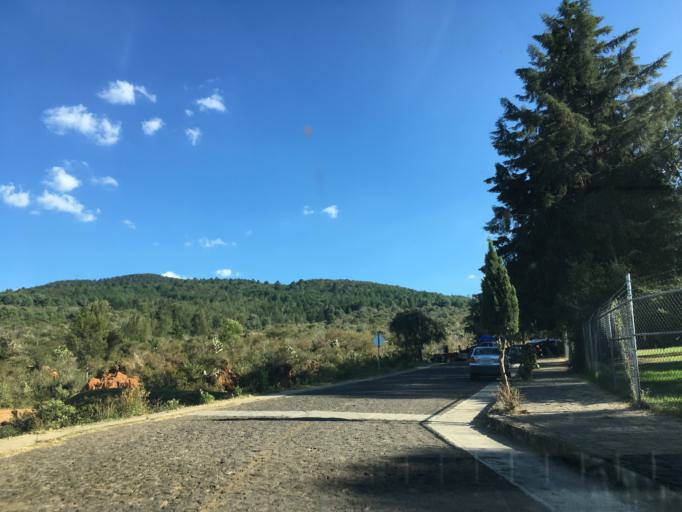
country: MX
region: Michoacan
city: Tzintzuntzan
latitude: 19.6252
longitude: -101.5716
